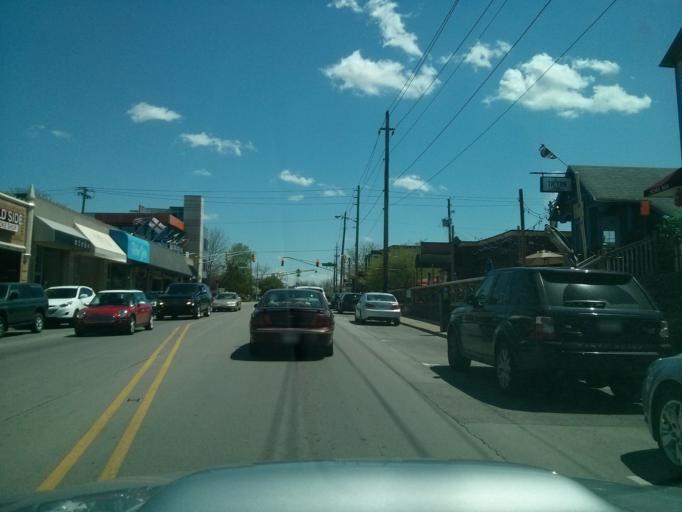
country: US
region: Indiana
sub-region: Marion County
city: Broad Ripple
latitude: 39.8697
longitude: -86.1426
